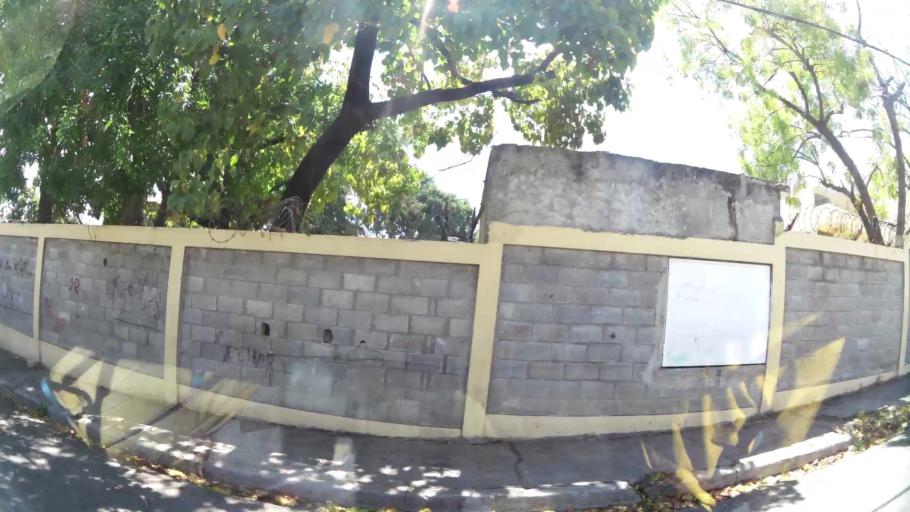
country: DO
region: San Cristobal
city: San Cristobal
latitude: 18.4057
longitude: -70.1128
